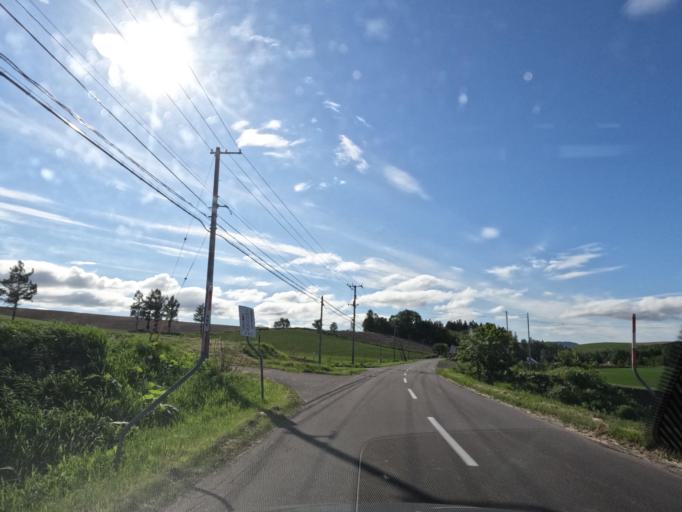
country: JP
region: Hokkaido
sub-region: Asahikawa-shi
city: Asahikawa
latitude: 43.5980
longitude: 142.4309
